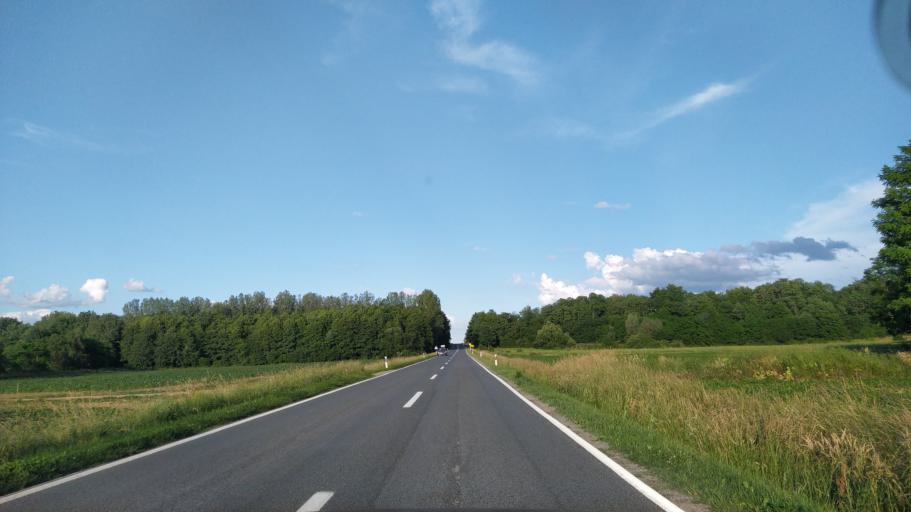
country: HR
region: Virovitick-Podravska
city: Cacinci
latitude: 45.5997
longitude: 17.8434
